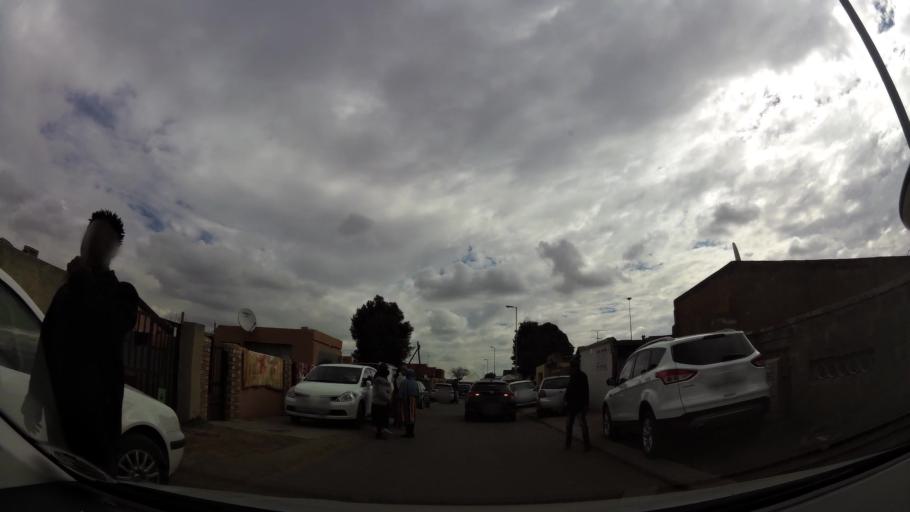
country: ZA
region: Gauteng
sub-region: City of Johannesburg Metropolitan Municipality
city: Soweto
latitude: -26.2790
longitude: 27.8602
